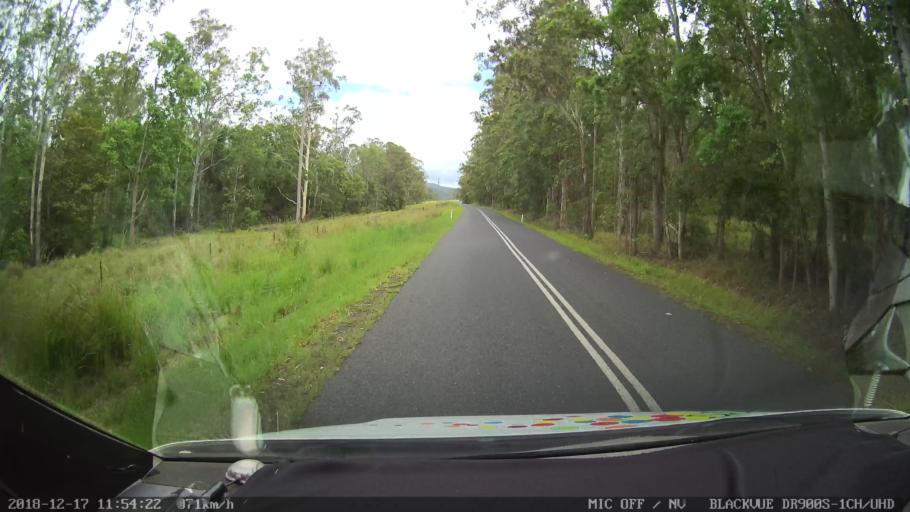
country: AU
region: New South Wales
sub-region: Kyogle
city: Kyogle
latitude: -28.5668
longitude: 152.5836
